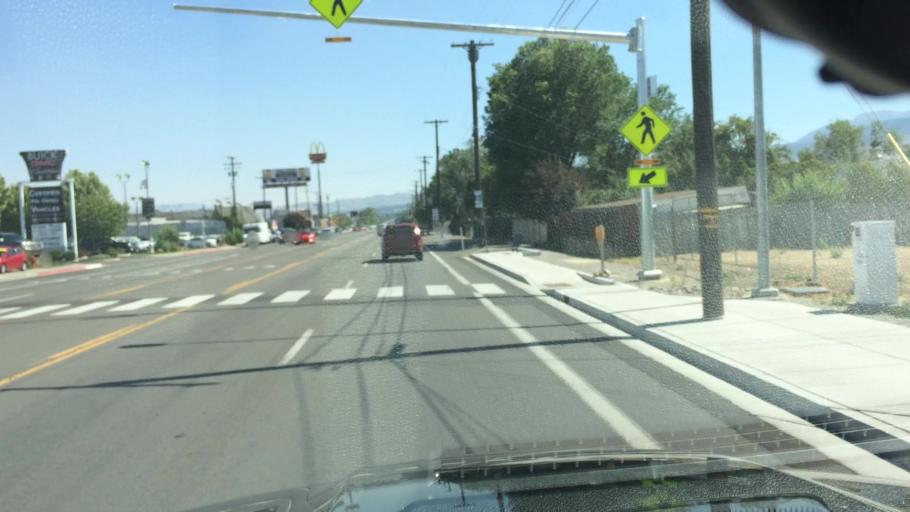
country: US
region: Nevada
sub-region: Washoe County
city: Reno
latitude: 39.5171
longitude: -119.7893
